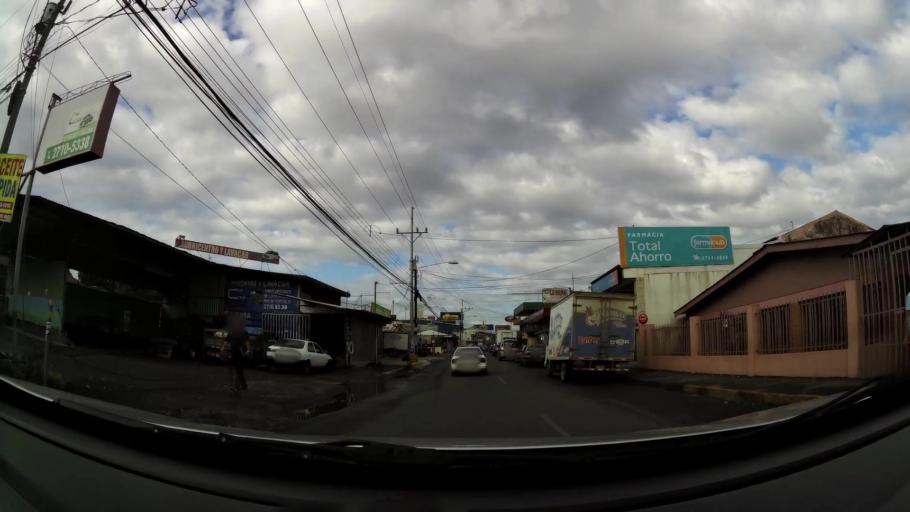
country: CR
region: Limon
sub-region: Canton de Pococi
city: Guapiles
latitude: 10.2154
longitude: -83.7833
